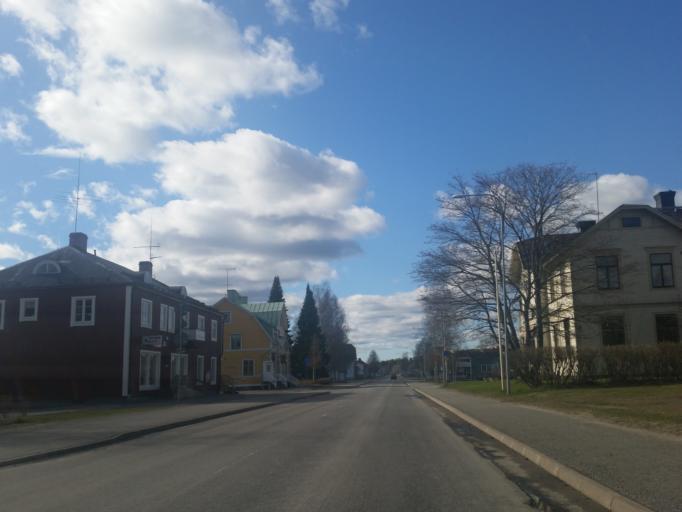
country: SE
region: Vaesterbotten
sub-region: Robertsfors Kommun
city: Robertsfors
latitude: 64.1895
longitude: 20.8561
